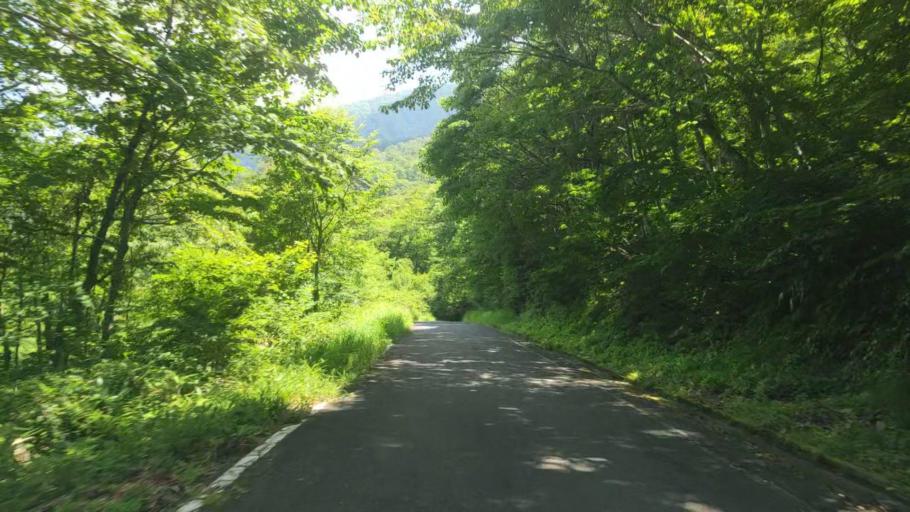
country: JP
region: Fukui
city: Ono
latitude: 35.7742
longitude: 136.5283
